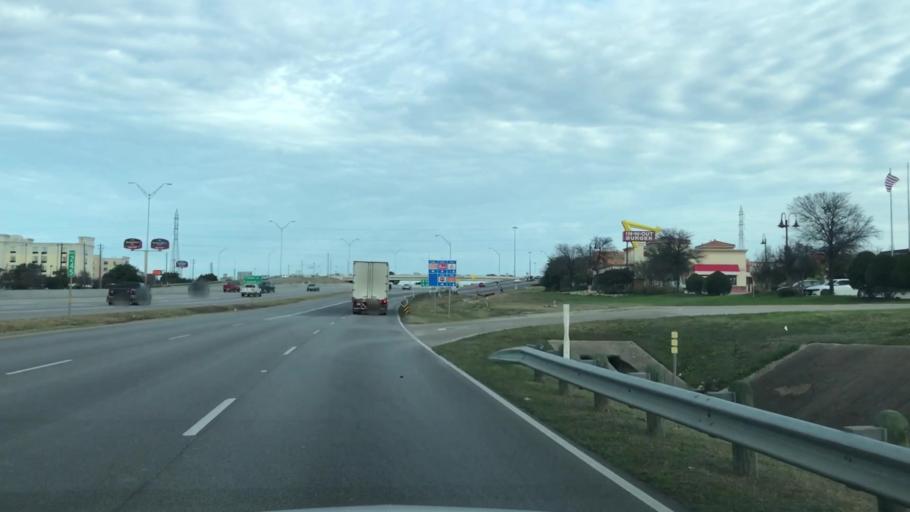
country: US
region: Texas
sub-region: Travis County
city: Wells Branch
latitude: 30.4038
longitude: -97.6747
